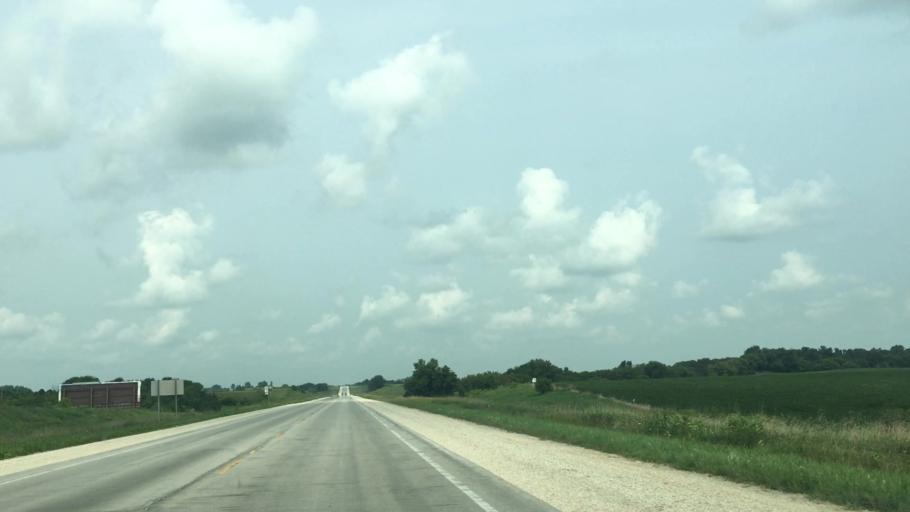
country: US
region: Iowa
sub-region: Winneshiek County
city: Decorah
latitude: 43.3691
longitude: -91.8079
